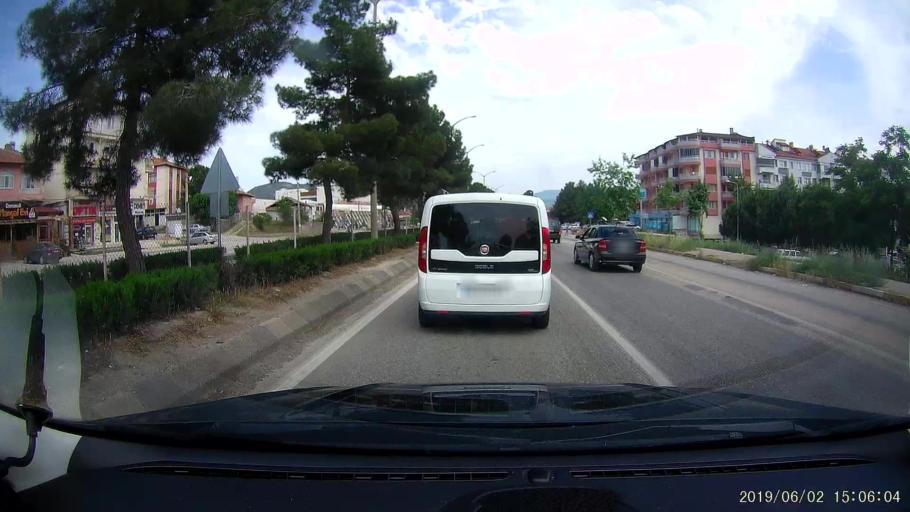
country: TR
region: Corum
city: Osmancik
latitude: 40.9795
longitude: 34.8010
